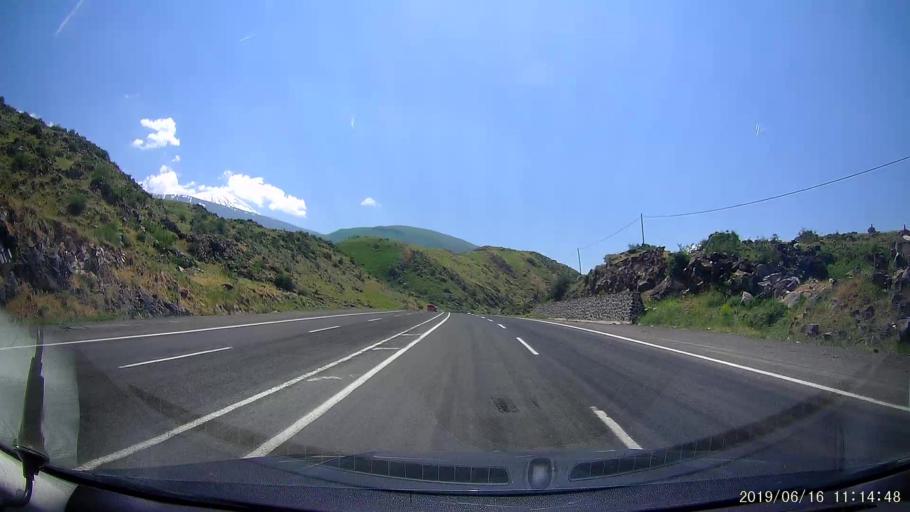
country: TR
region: Igdir
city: Igdir
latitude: 39.7732
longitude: 44.1418
